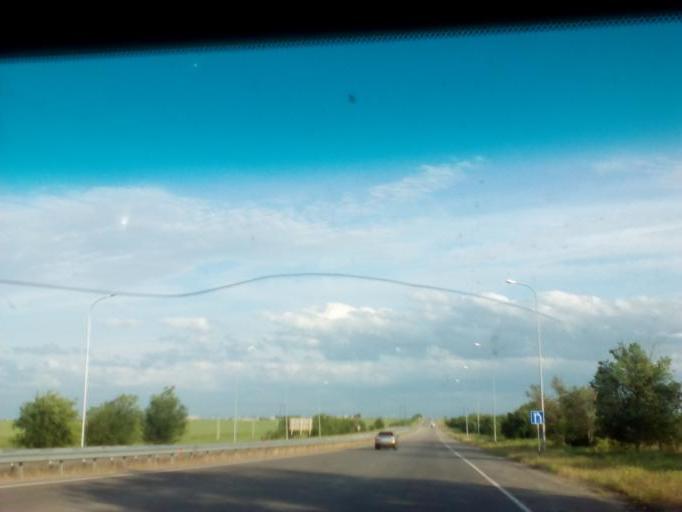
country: KZ
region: Ongtustik Qazaqstan
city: Temirlanovka
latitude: 42.5251
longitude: 69.3442
